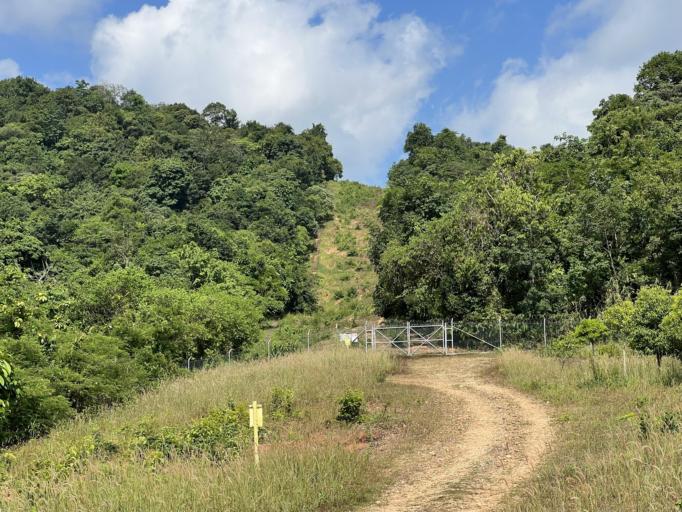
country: MM
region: Tanintharyi
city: Dawei
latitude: 14.6044
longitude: 97.9729
